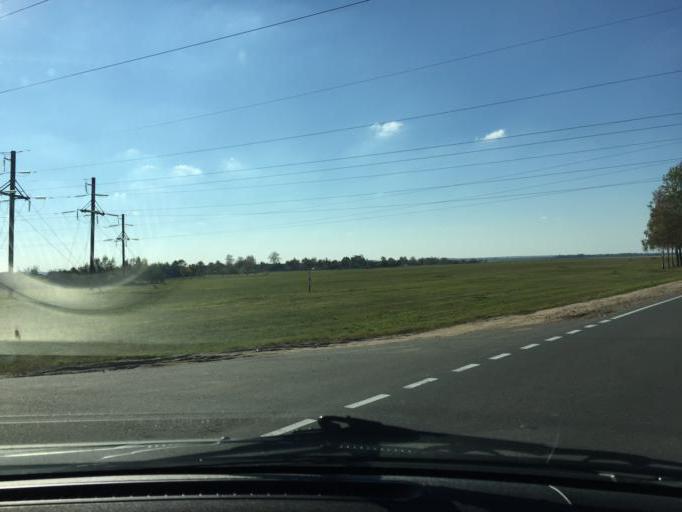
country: BY
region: Minsk
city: Salihorsk
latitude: 52.8534
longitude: 27.4642
